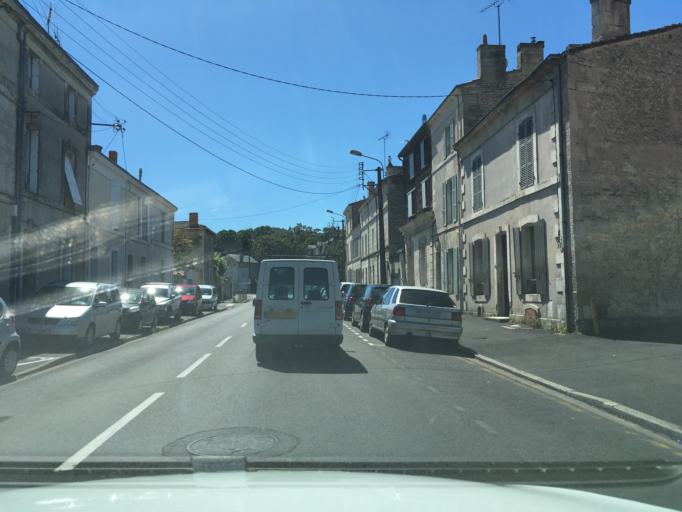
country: FR
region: Poitou-Charentes
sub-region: Departement des Deux-Sevres
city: Niort
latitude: 46.3235
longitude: -0.4533
